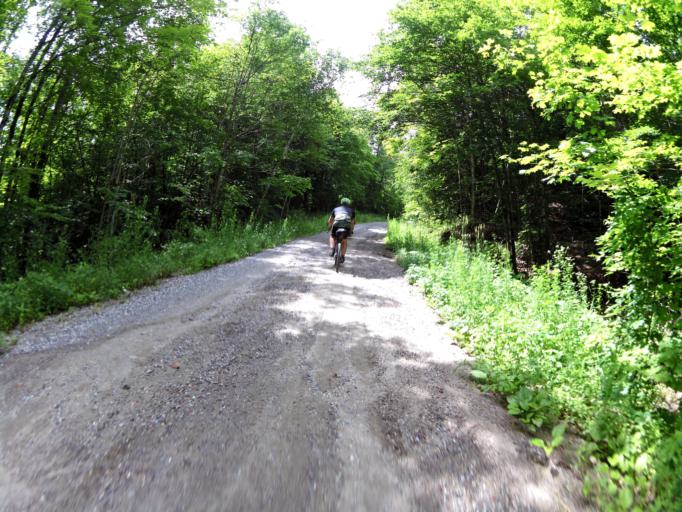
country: CA
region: Ontario
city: Perth
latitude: 45.0189
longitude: -76.5793
